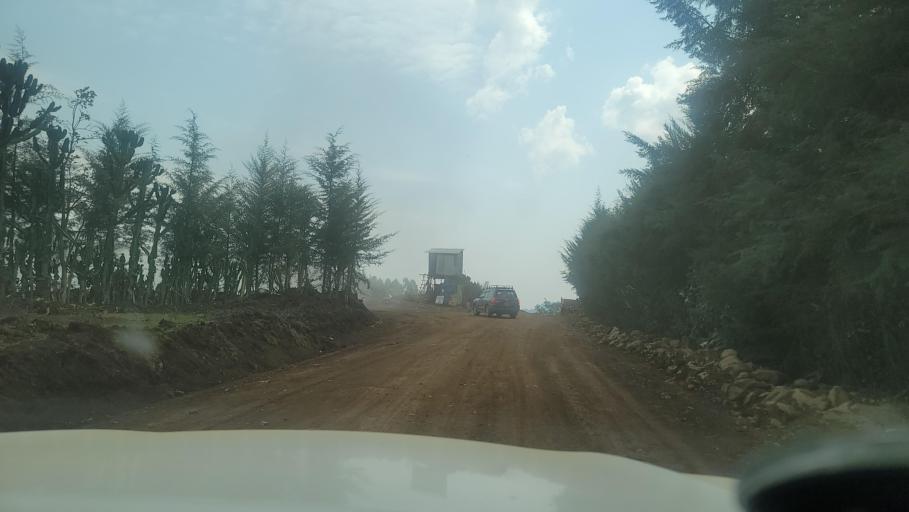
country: ET
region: Oromiya
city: Agaro
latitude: 7.7363
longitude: 36.2627
